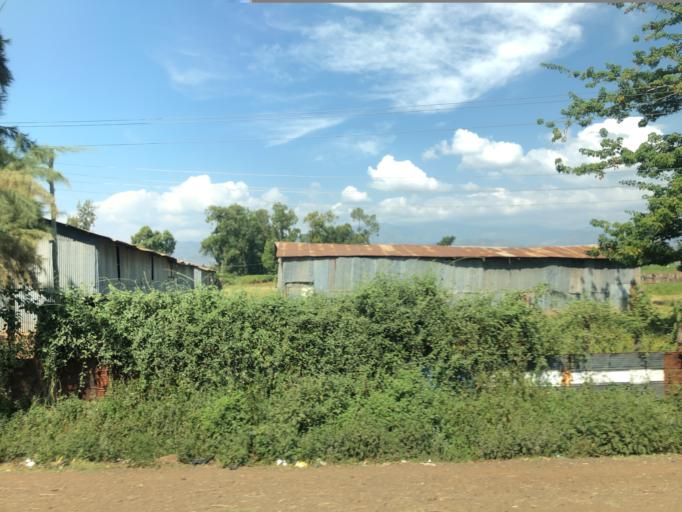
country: ET
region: Southern Nations, Nationalities, and People's Region
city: Arba Minch'
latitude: 5.8665
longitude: 37.4789
